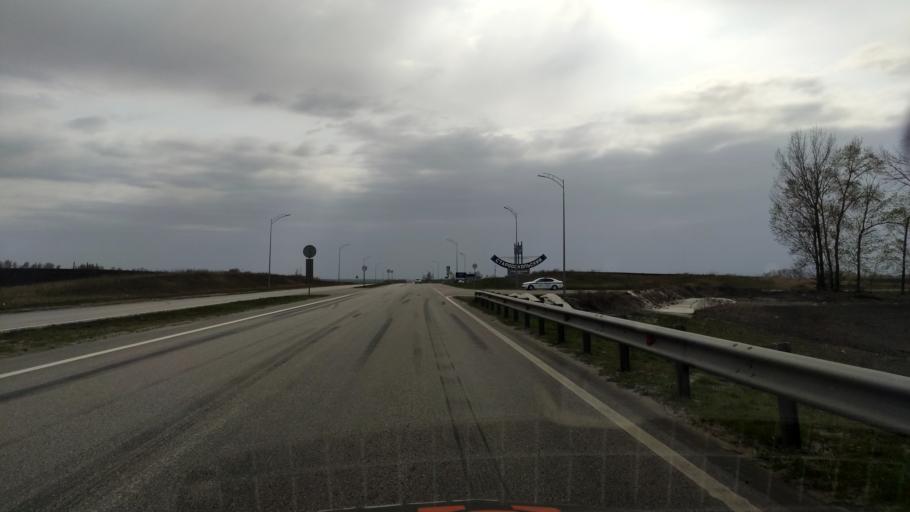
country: RU
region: Belgorod
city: Staryy Oskol
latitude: 51.4229
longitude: 37.8931
